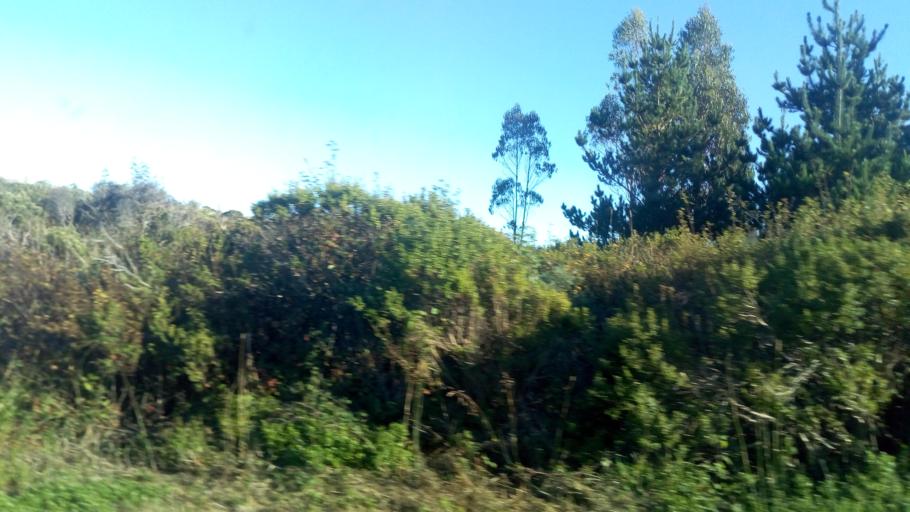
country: US
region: California
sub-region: Marin County
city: Inverness
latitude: 38.0358
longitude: -122.8760
